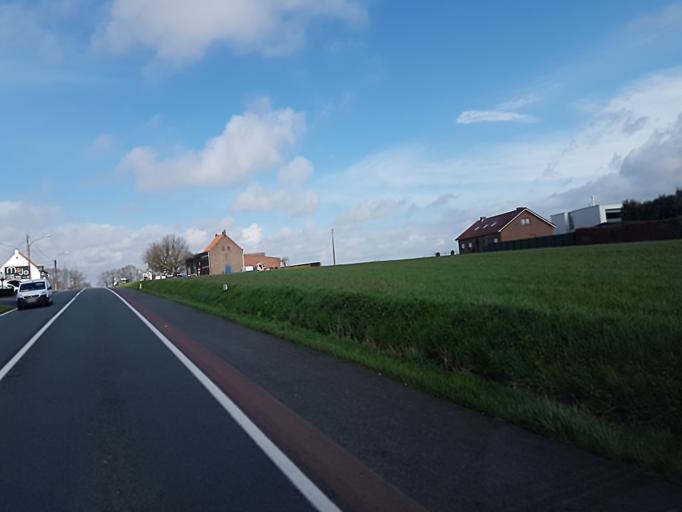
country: BE
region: Flanders
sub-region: Provincie Oost-Vlaanderen
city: Kruishoutem
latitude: 50.8896
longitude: 3.5413
